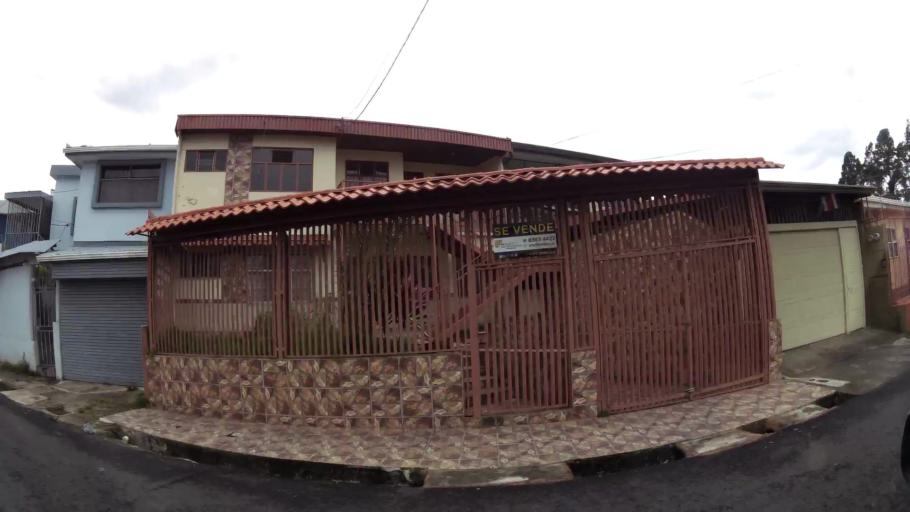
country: CR
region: San Jose
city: San Vicente de Moravia
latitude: 9.9612
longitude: -84.0519
